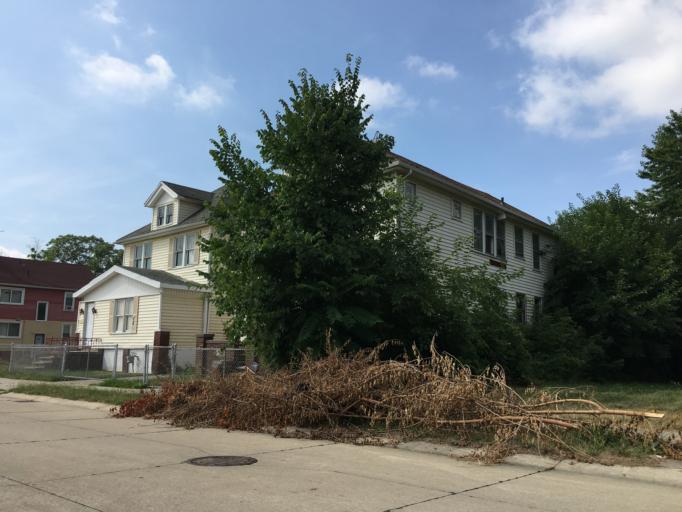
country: US
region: Michigan
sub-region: Wayne County
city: Grosse Pointe Park
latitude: 42.3611
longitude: -82.9741
